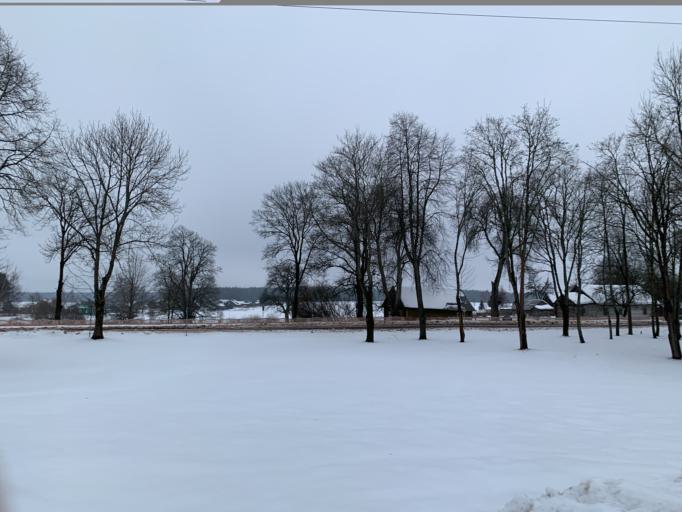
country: BY
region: Minsk
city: Kryvichy
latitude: 54.5898
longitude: 27.2070
